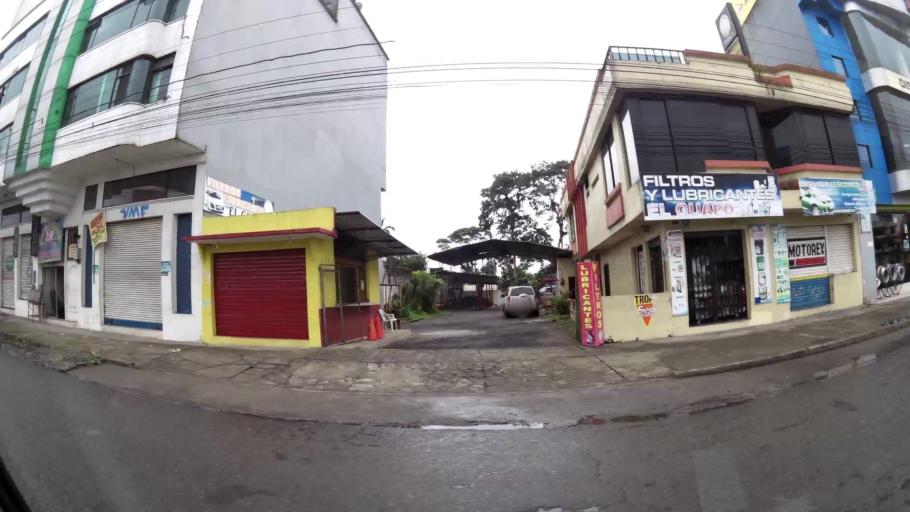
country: EC
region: Santo Domingo de los Tsachilas
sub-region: Canton Santo Domingo de los Colorados
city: Santo Domingo de los Colorados
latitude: -0.2686
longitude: -79.1945
